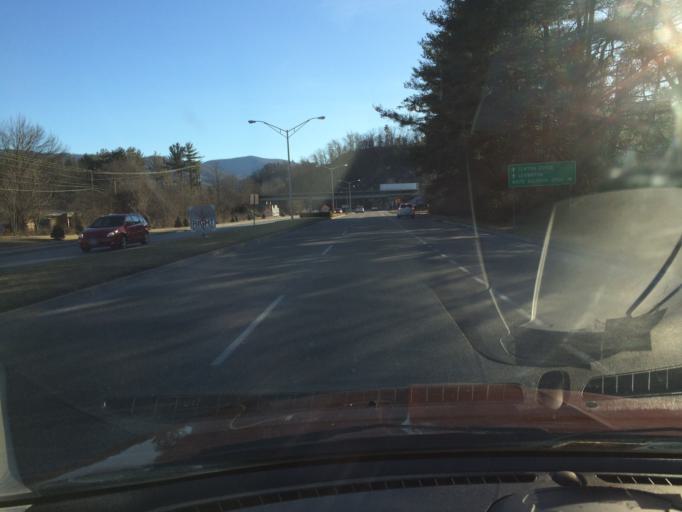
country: US
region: Virginia
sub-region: City of Covington
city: Fairlawn
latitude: 37.7756
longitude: -79.9921
